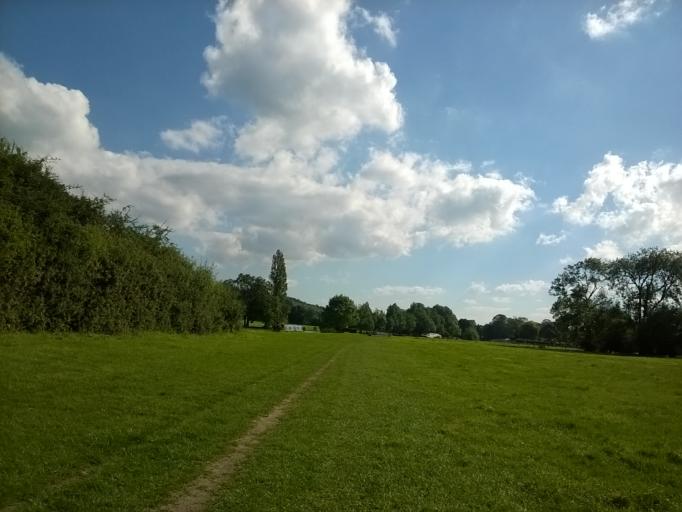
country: GB
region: England
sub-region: West Berkshire
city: Tilehurst
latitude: 51.4895
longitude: -1.0441
